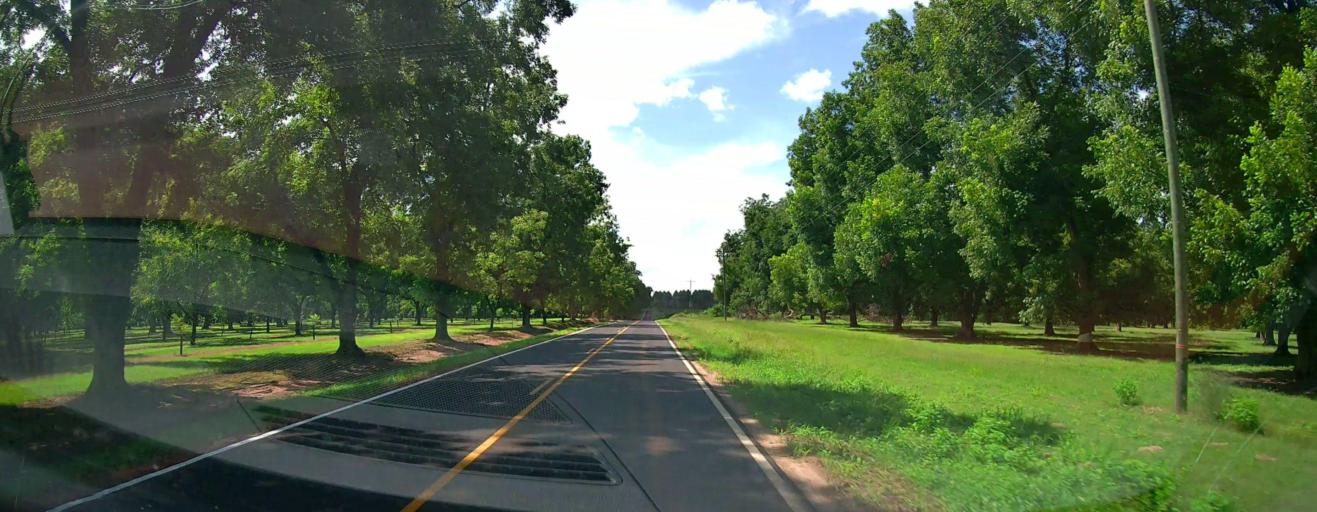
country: US
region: Georgia
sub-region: Macon County
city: Marshallville
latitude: 32.4727
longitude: -83.8845
